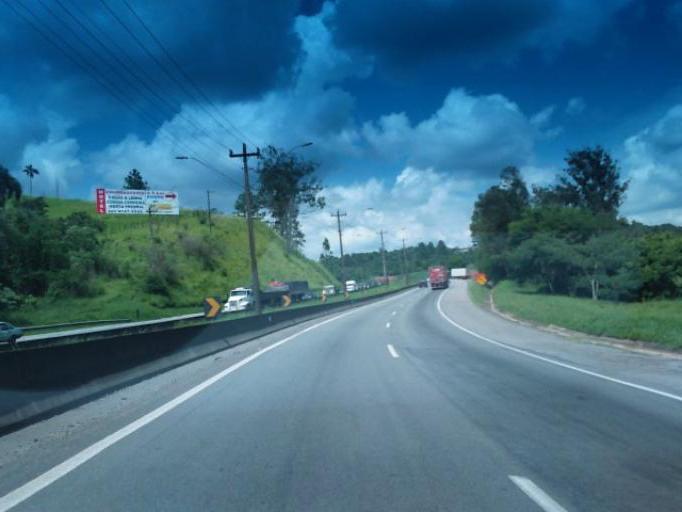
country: BR
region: Sao Paulo
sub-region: Itapecerica Da Serra
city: Itapecerica da Serra
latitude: -23.7224
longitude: -46.8888
